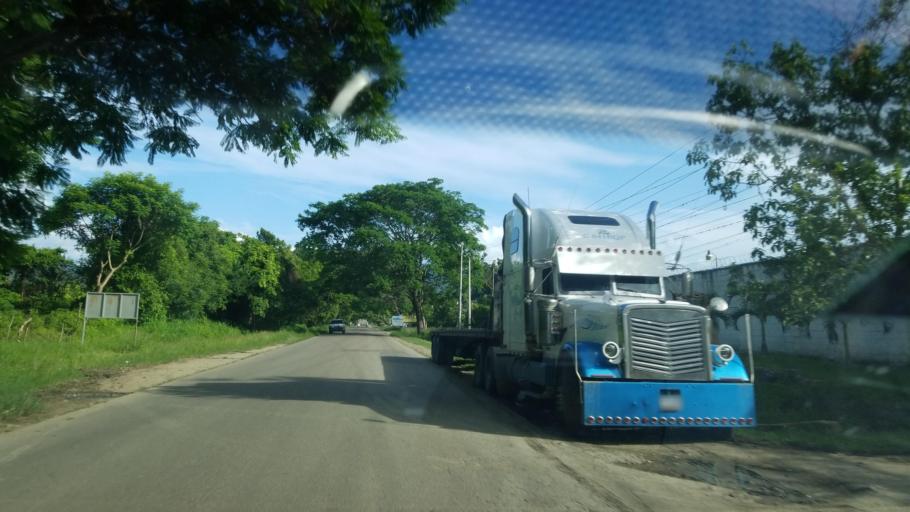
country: HN
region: El Paraiso
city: Cuyali
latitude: 13.8941
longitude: -86.5552
